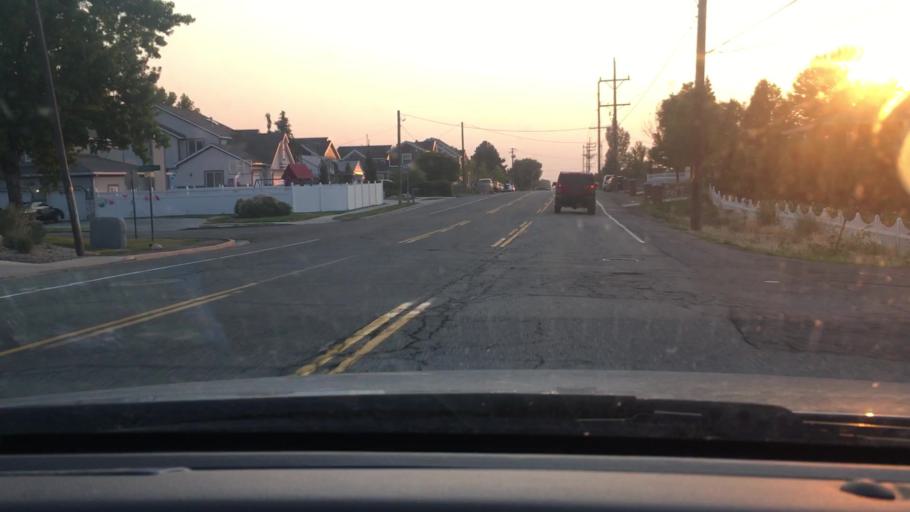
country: US
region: Utah
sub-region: Salt Lake County
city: East Millcreek
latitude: 40.6871
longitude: -111.8195
